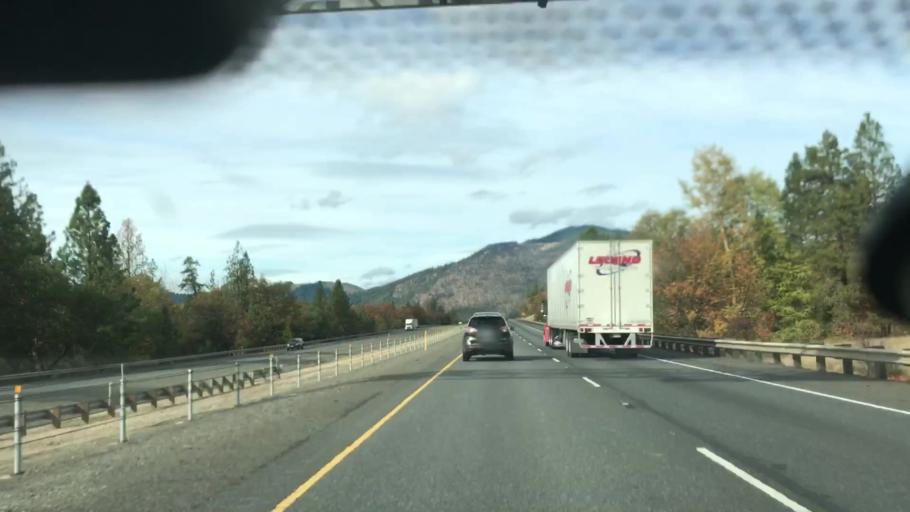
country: US
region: Oregon
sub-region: Josephine County
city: Merlin
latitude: 42.5368
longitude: -123.3698
